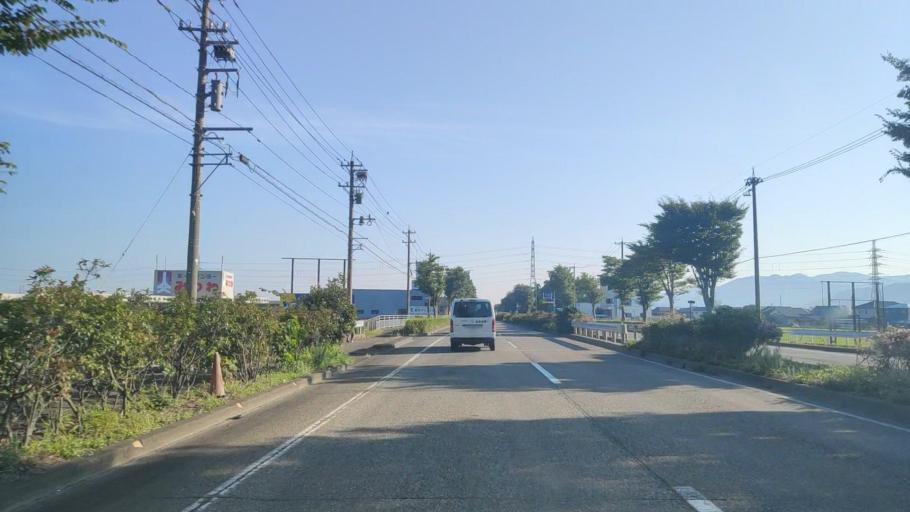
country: JP
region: Fukui
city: Maruoka
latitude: 36.1340
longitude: 136.2621
